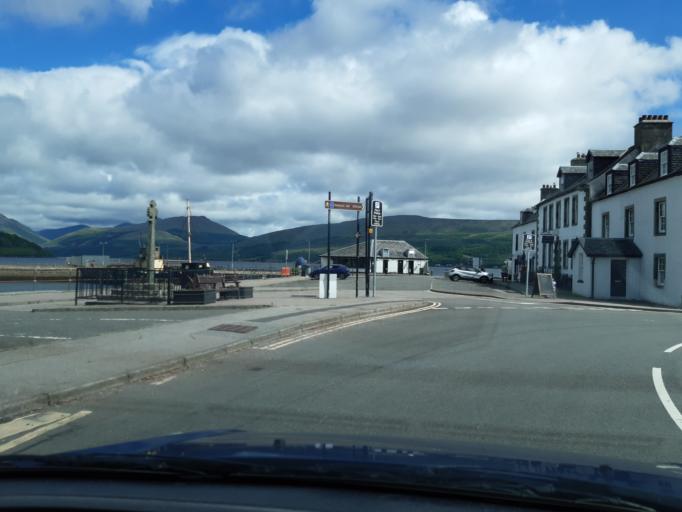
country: GB
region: Scotland
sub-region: Argyll and Bute
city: Garelochhead
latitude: 56.2314
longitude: -5.0724
